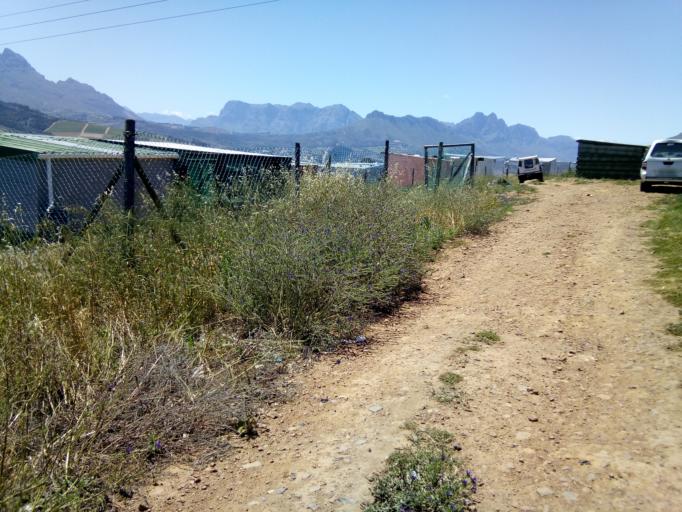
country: ZA
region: Western Cape
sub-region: Cape Winelands District Municipality
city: Stellenbosch
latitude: -33.9211
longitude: 18.8343
